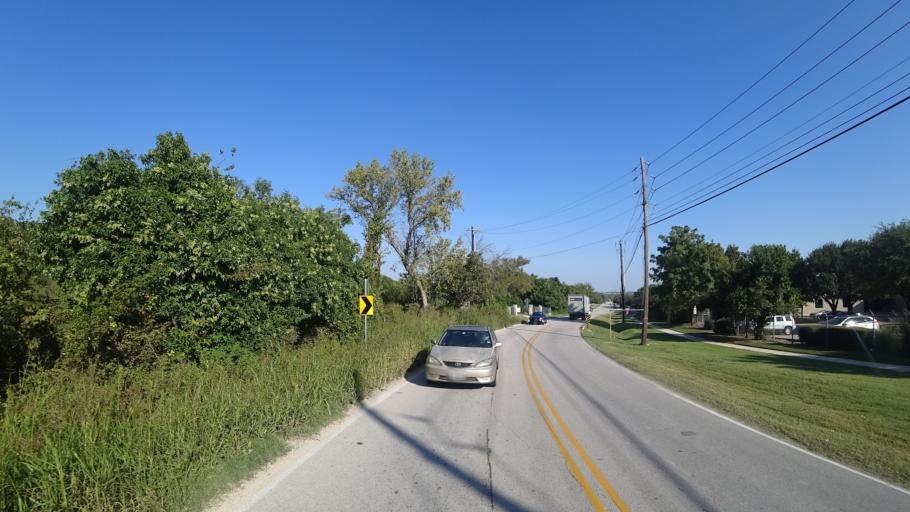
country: US
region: Texas
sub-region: Travis County
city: Wells Branch
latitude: 30.3454
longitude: -97.6703
